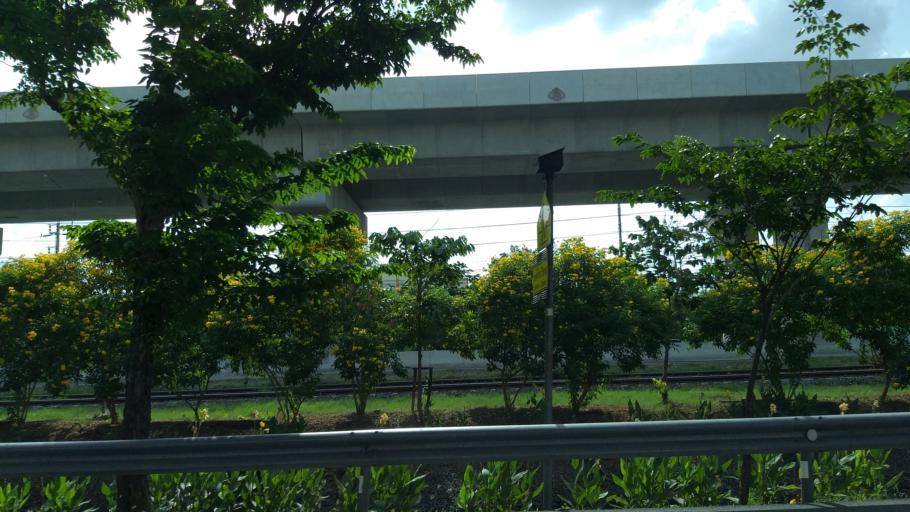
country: TH
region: Bangkok
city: Don Mueang
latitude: 13.9301
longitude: 100.6070
